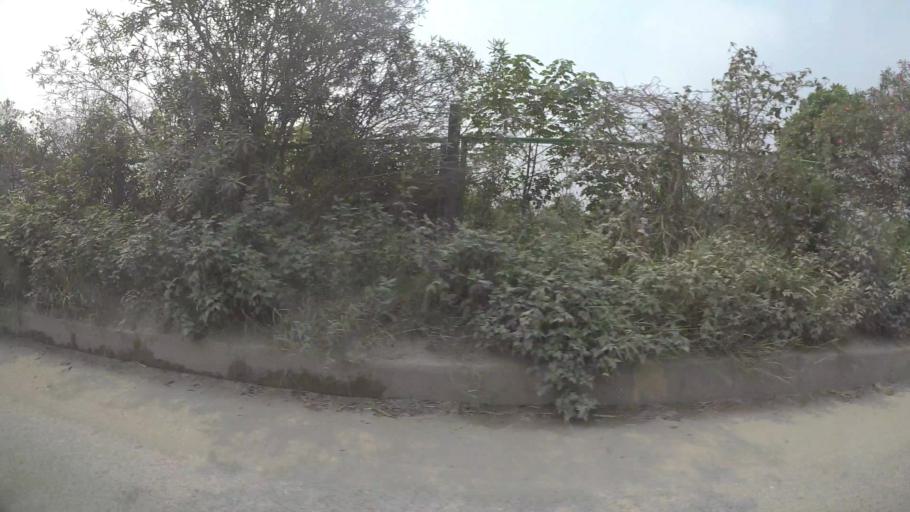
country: VN
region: Ha Noi
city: Troi
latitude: 21.0093
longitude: 105.7057
